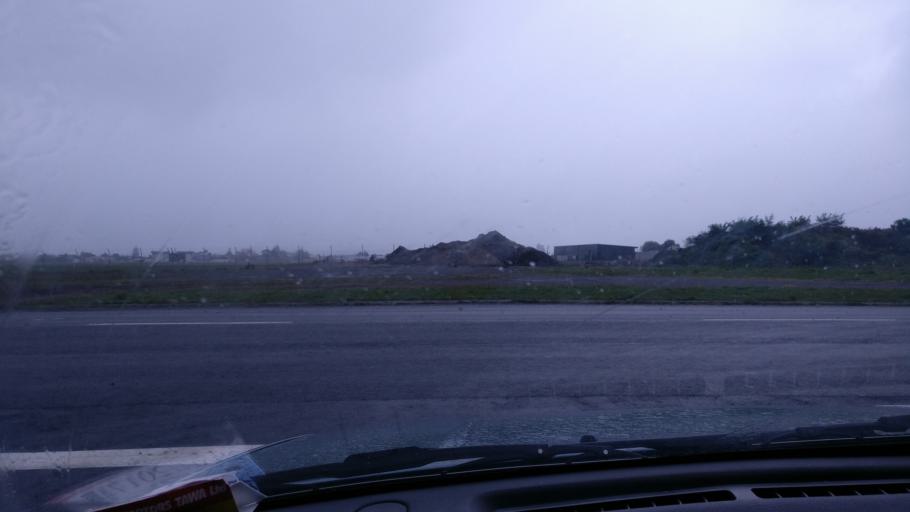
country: NZ
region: Wellington
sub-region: Kapiti Coast District
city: Paraparaumu
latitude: -40.9049
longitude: 174.9935
